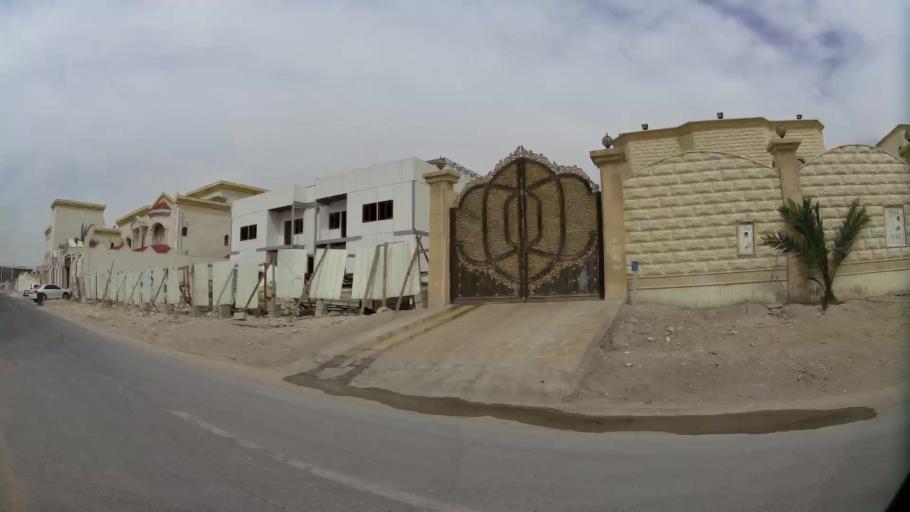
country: QA
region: Baladiyat ar Rayyan
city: Ar Rayyan
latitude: 25.2058
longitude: 51.4511
